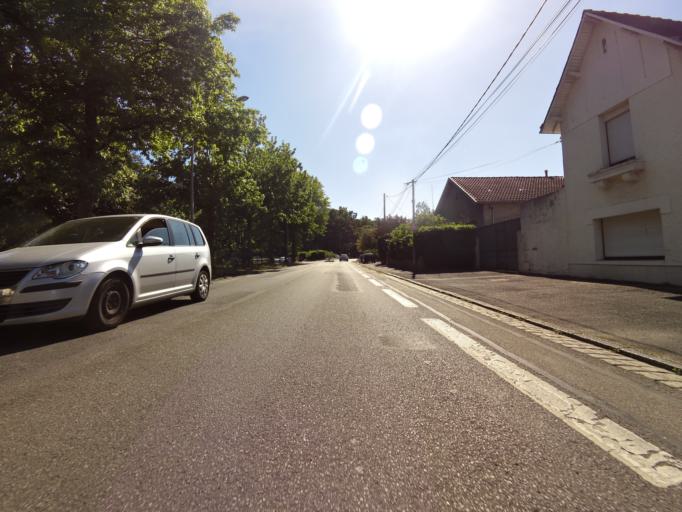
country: FR
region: Pays de la Loire
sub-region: Departement de la Loire-Atlantique
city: Nantes
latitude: 47.2524
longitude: -1.5628
